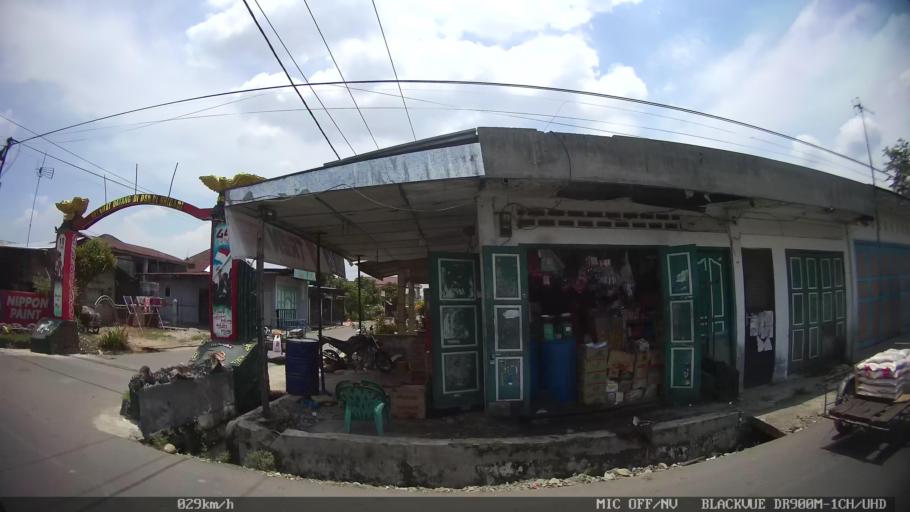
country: ID
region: North Sumatra
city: Sunggal
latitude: 3.5947
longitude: 98.5518
